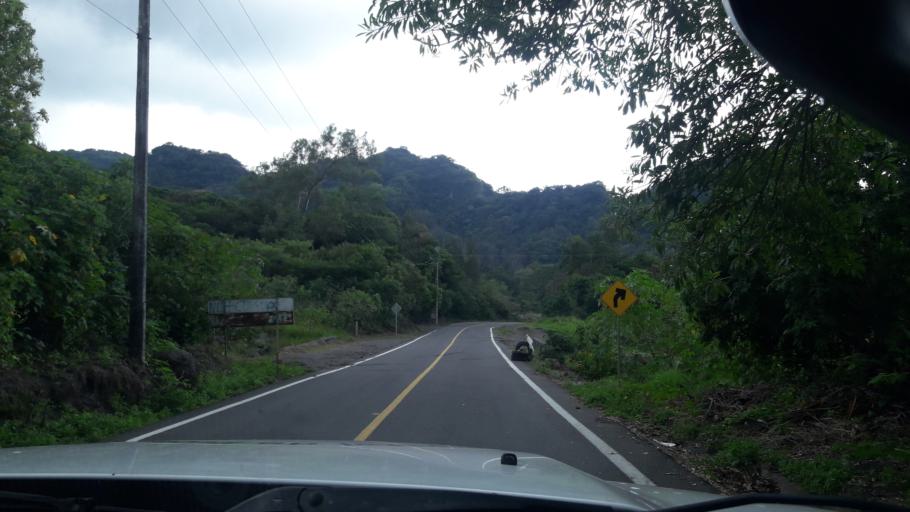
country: MX
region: Colima
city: Suchitlan
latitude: 19.4541
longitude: -103.7139
